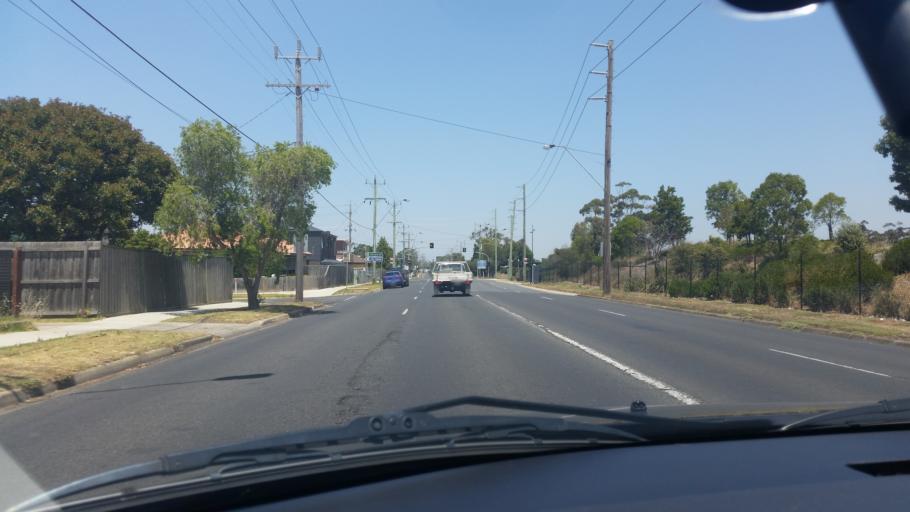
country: AU
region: Victoria
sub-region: Greater Geelong
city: Bell Park
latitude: -38.1205
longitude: 144.3415
